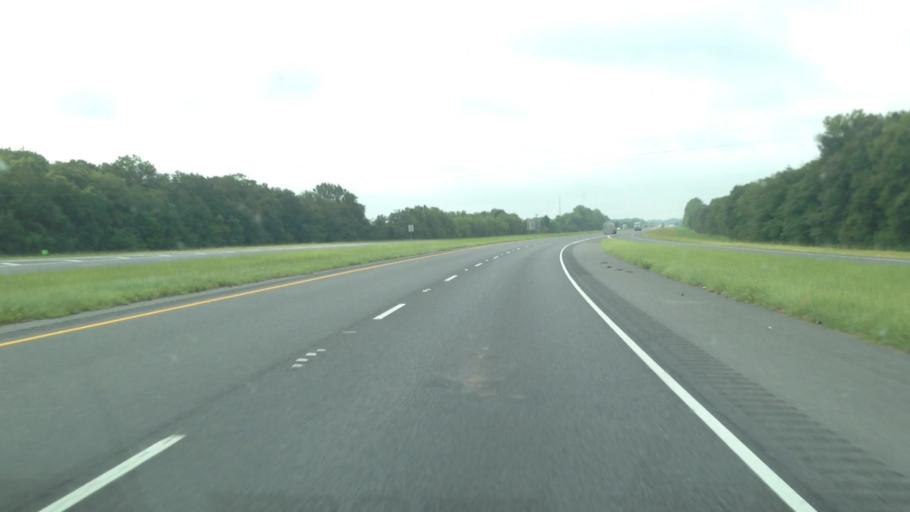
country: US
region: Louisiana
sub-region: Saint Landry Parish
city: Opelousas
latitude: 30.6392
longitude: -92.0487
